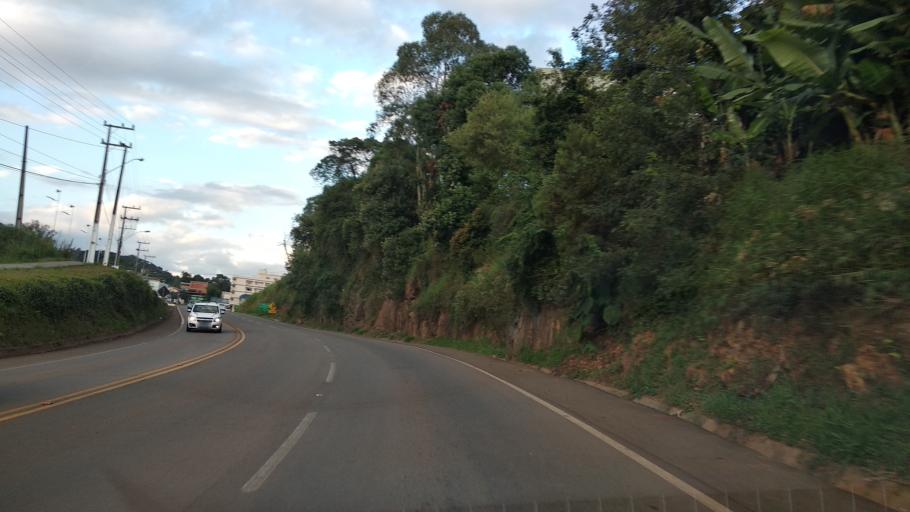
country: BR
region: Santa Catarina
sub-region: Videira
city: Videira
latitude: -27.0016
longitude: -51.1231
